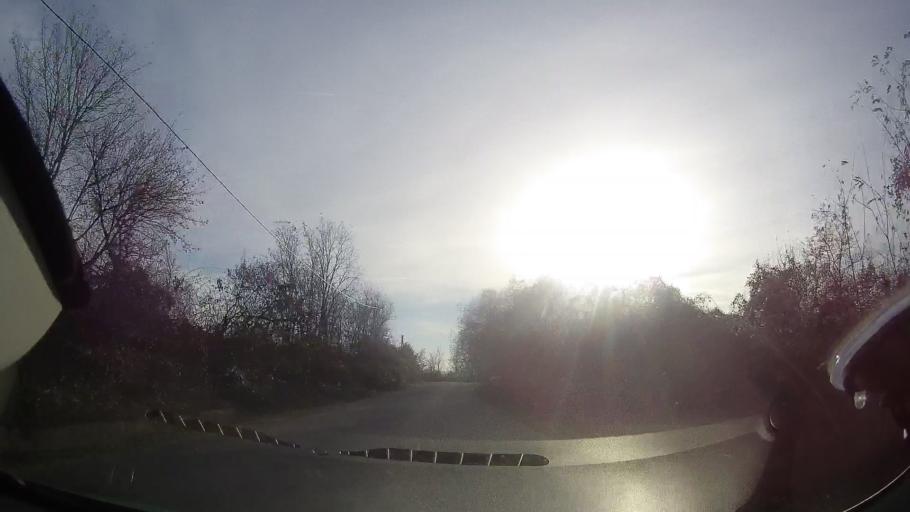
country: RO
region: Bihor
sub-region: Comuna Sarbi
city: Burzuc
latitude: 47.1184
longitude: 22.1793
